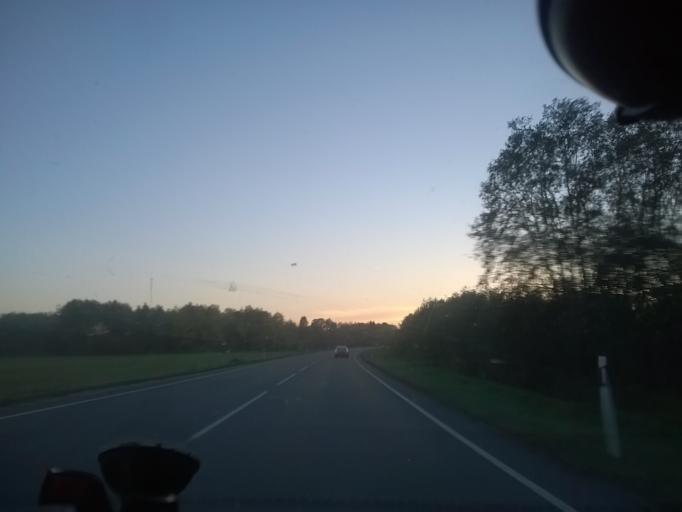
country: EE
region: Laeaene
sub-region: Ridala Parish
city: Uuemoisa
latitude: 58.9608
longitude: 23.8196
